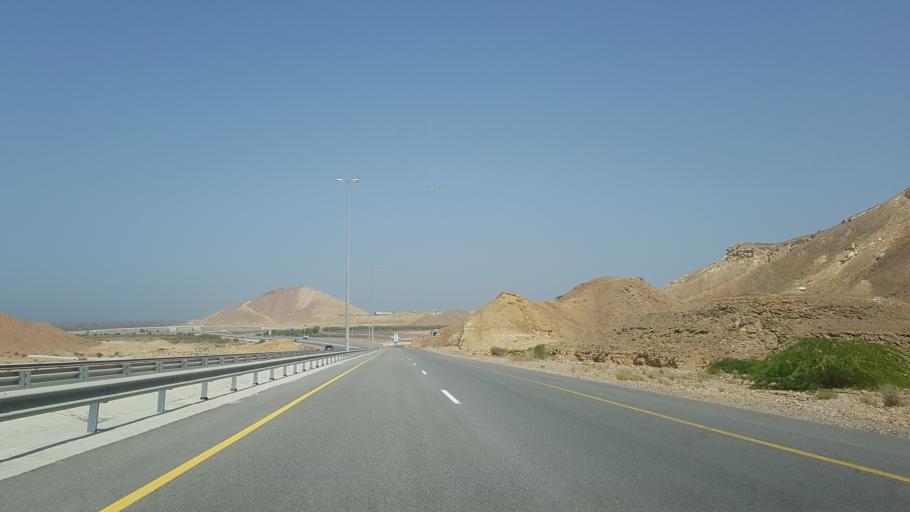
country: OM
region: Muhafazat Masqat
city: Muscat
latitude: 23.2065
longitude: 58.9129
